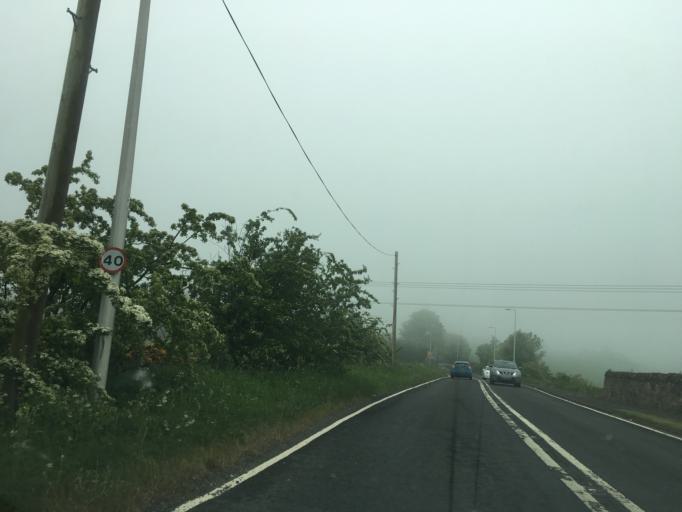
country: GB
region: Scotland
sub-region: Midlothian
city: Penicuik
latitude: 55.8301
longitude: -3.2019
